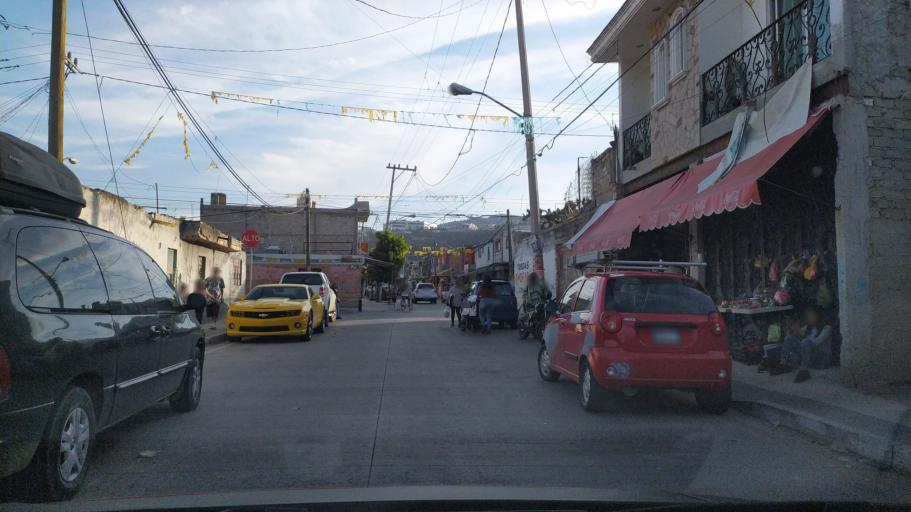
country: MX
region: Jalisco
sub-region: Tlajomulco de Zuniga
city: Palomar
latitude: 20.6240
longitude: -103.4562
